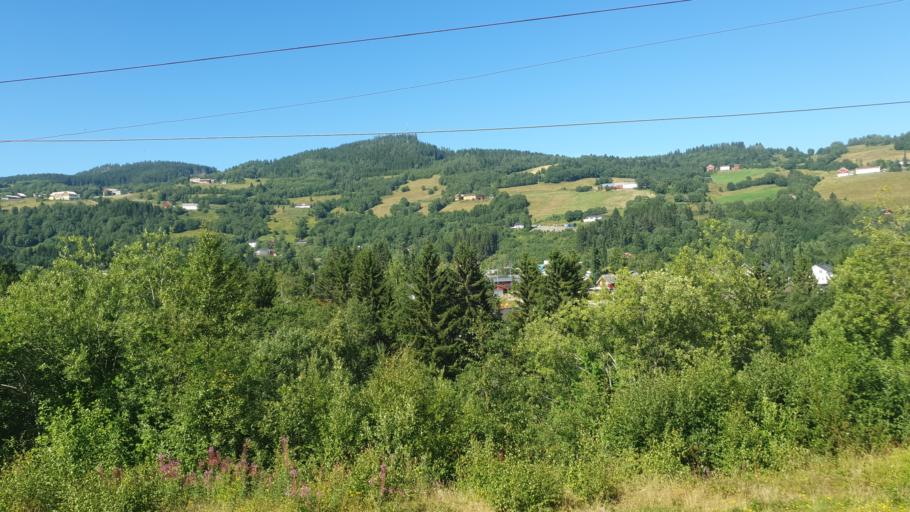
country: NO
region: Sor-Trondelag
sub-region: Meldal
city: Meldal
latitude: 63.1682
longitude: 9.7465
